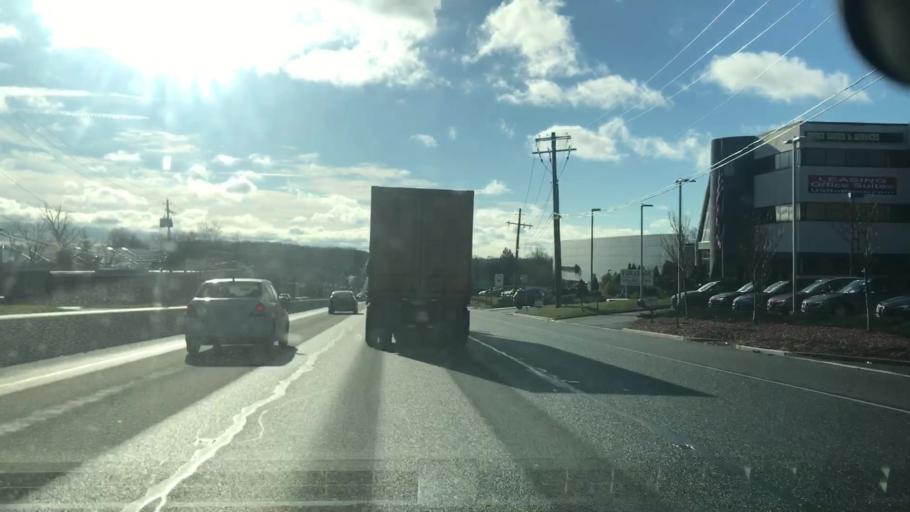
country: US
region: New Jersey
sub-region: Bergen County
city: Allendale
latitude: 41.0526
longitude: -74.1193
